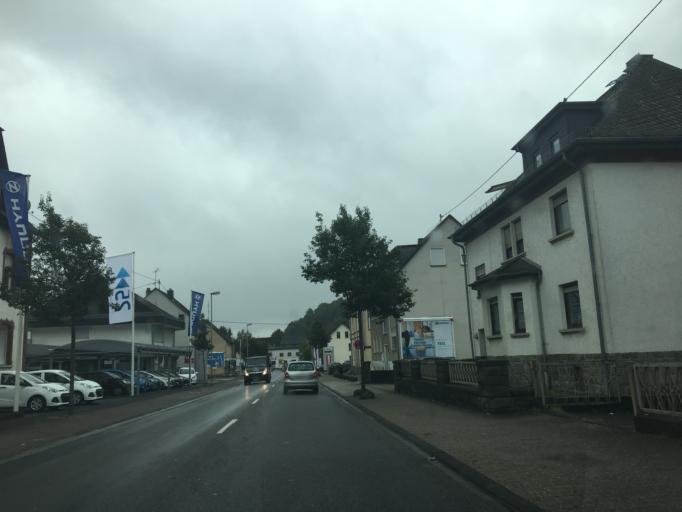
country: DE
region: Rheinland-Pfalz
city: Montabaur
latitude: 50.4383
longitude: 7.8326
